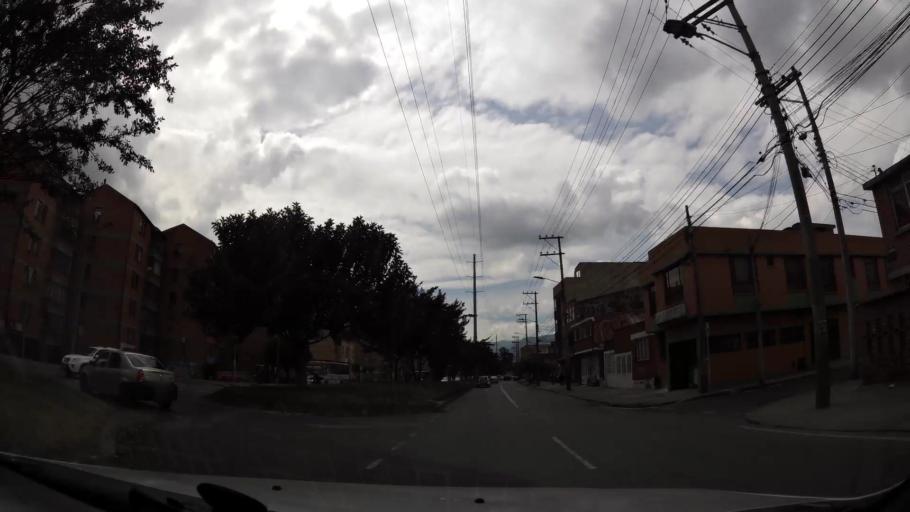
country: CO
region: Bogota D.C.
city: Bogota
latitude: 4.6114
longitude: -74.1106
